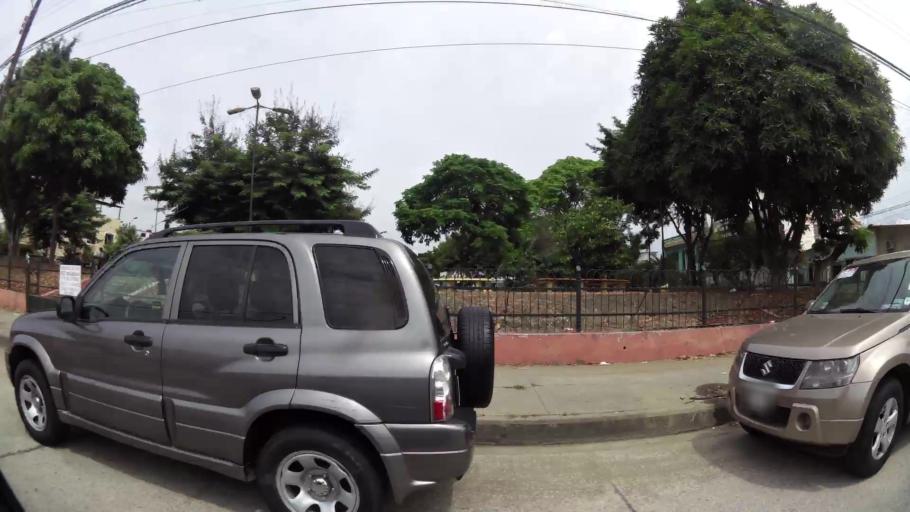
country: EC
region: Guayas
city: Eloy Alfaro
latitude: -2.1492
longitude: -79.8953
